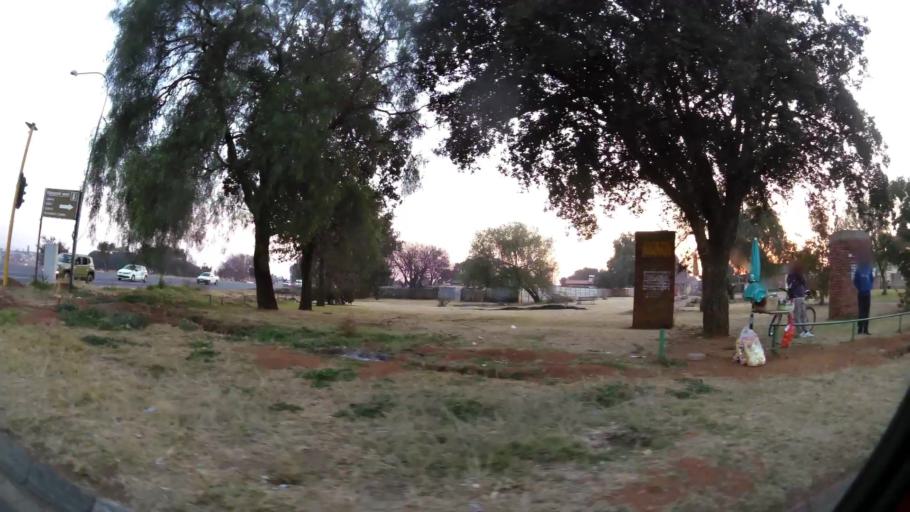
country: ZA
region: Gauteng
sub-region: City of Johannesburg Metropolitan Municipality
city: Soweto
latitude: -26.2916
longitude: 27.8806
